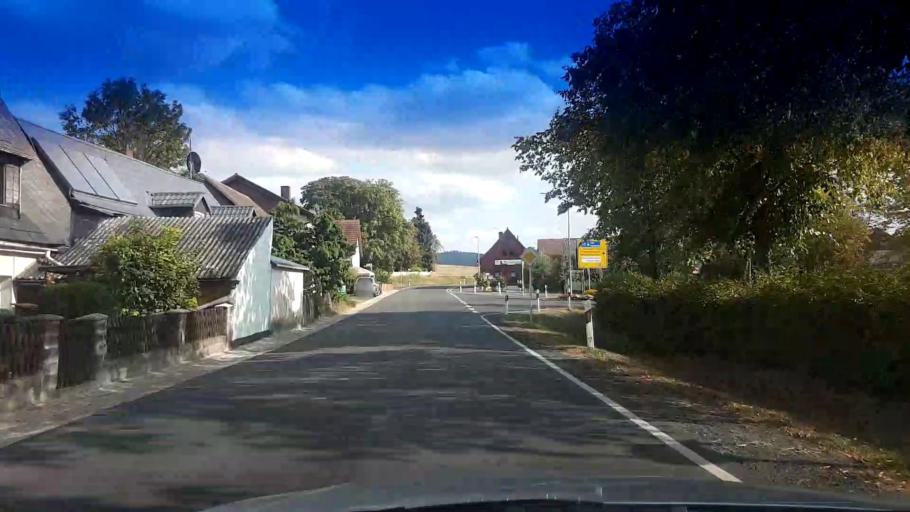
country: DE
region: Bavaria
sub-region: Upper Palatinate
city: Neualbenreuth
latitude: 49.9787
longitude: 12.4440
